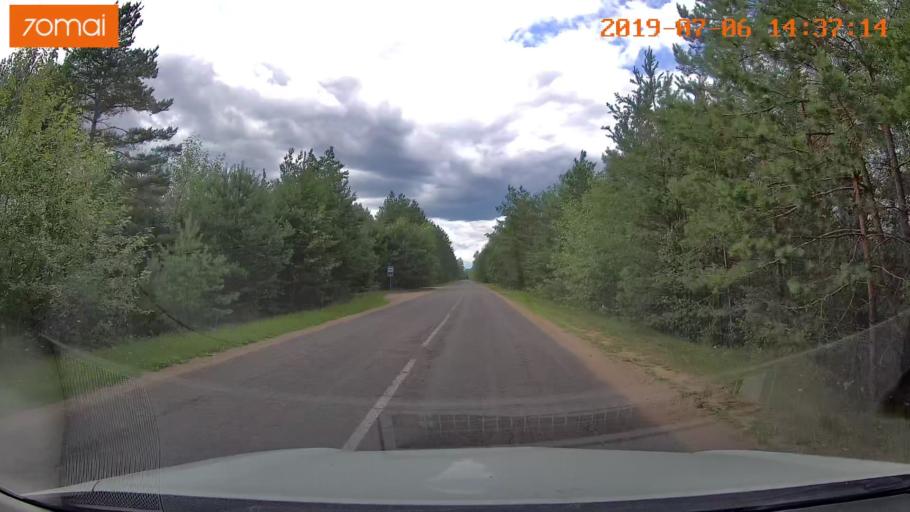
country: BY
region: Minsk
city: Ivyanyets
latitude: 53.8954
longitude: 26.7226
